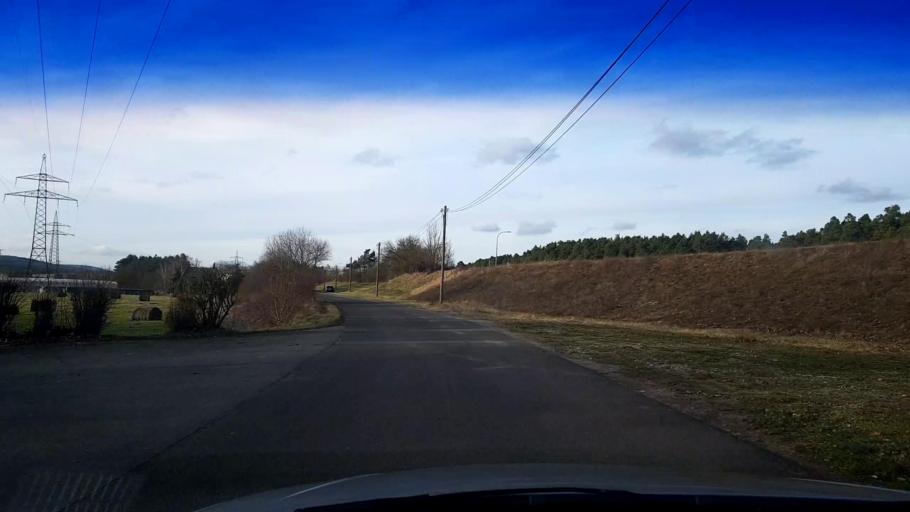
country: DE
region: Bavaria
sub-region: Upper Franconia
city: Strullendorf
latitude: 49.8334
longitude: 10.9614
